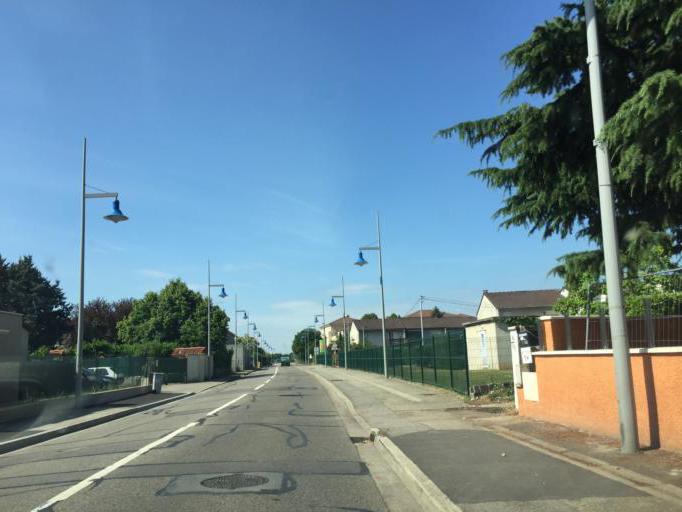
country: FR
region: Rhone-Alpes
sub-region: Departement du Rhone
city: Chassieu
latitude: 45.7369
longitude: 4.9682
